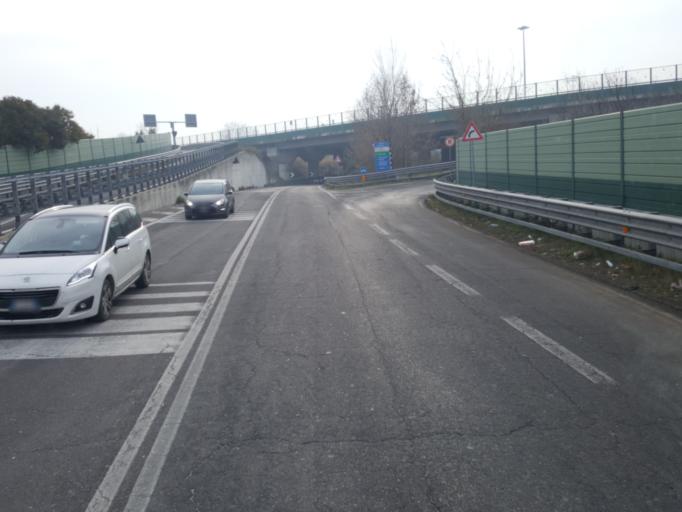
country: IT
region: Emilia-Romagna
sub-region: Forli-Cesena
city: Cesena
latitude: 44.1434
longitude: 12.2642
